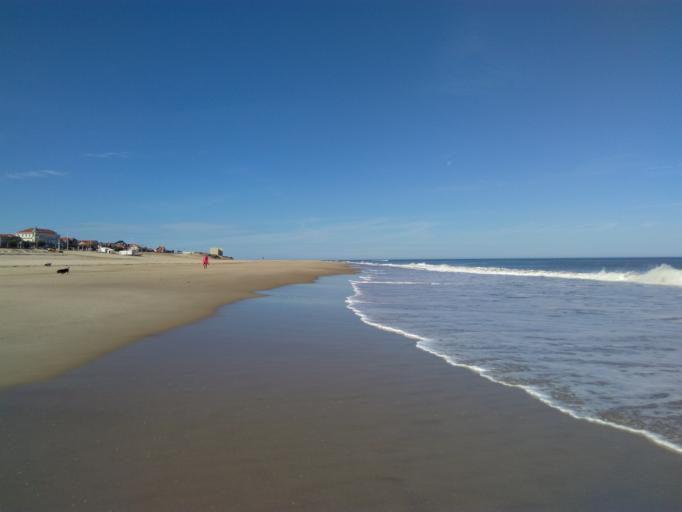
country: FR
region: Aquitaine
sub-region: Departement de la Gironde
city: Soulac-sur-Mer
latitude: 45.5199
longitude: -1.1259
